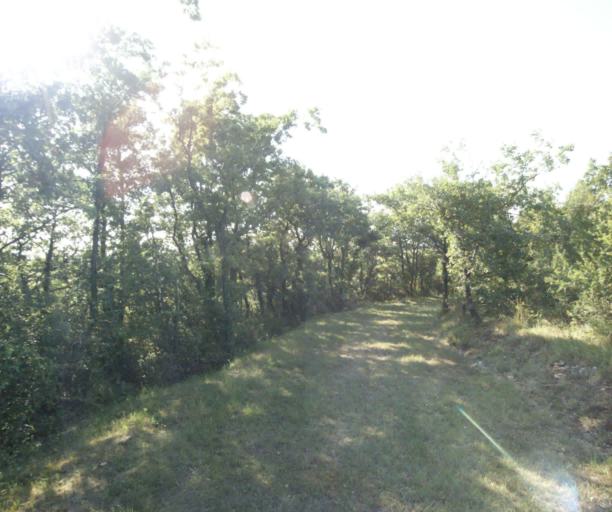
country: FR
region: Midi-Pyrenees
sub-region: Departement de la Haute-Garonne
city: Saint-Felix-Lauragais
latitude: 43.4445
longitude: 1.8207
